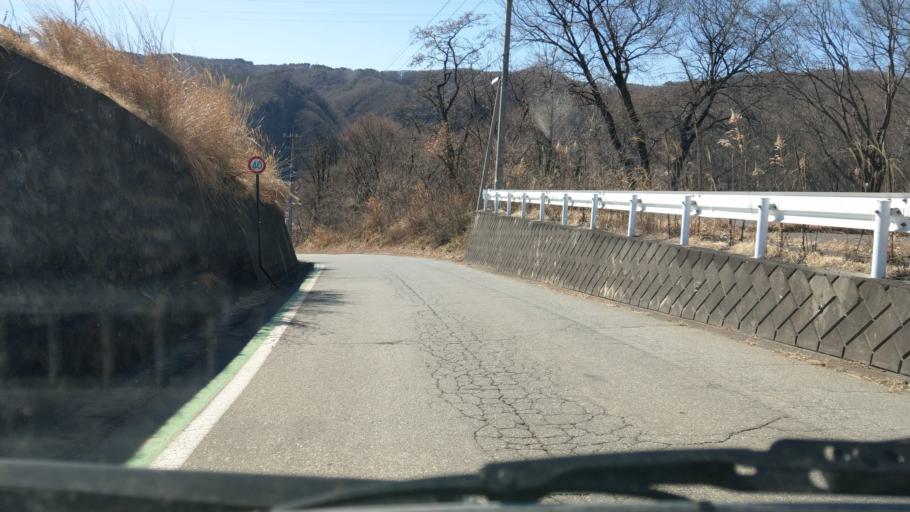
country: JP
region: Nagano
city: Komoro
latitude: 36.3370
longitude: 138.3933
